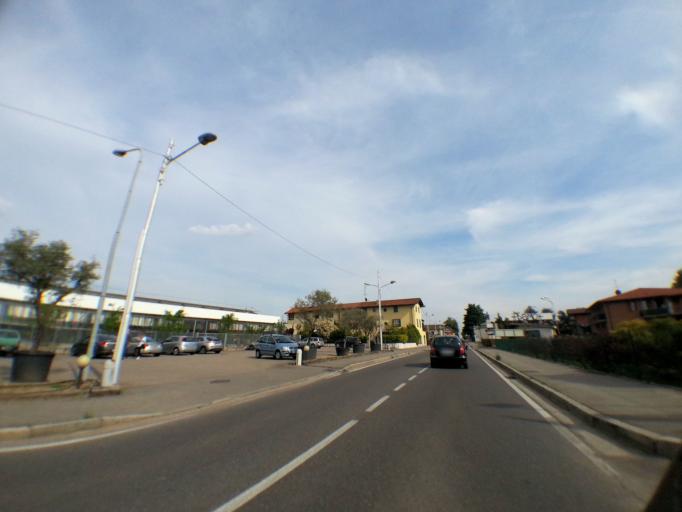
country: IT
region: Lombardy
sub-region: Provincia di Como
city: Cermenate
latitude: 45.7140
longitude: 9.0796
